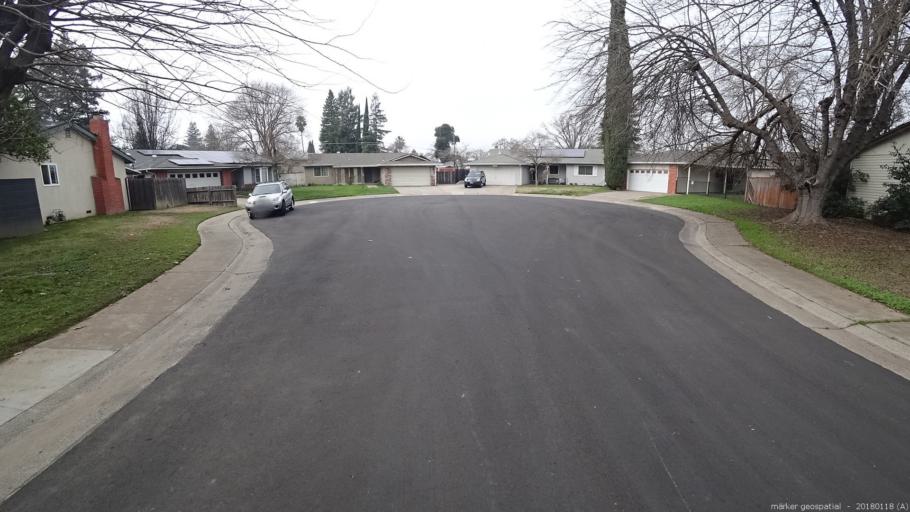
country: US
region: California
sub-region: Sacramento County
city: Rancho Cordova
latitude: 38.5926
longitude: -121.3171
